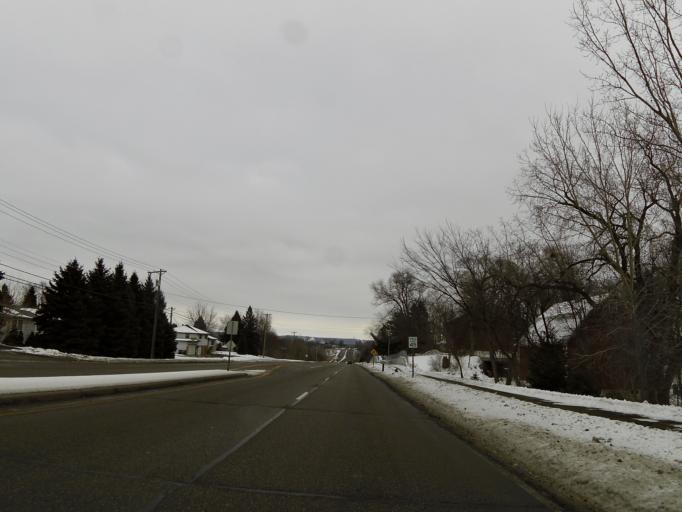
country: US
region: Minnesota
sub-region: Dakota County
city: Inver Grove Heights
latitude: 44.8478
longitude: -93.0543
